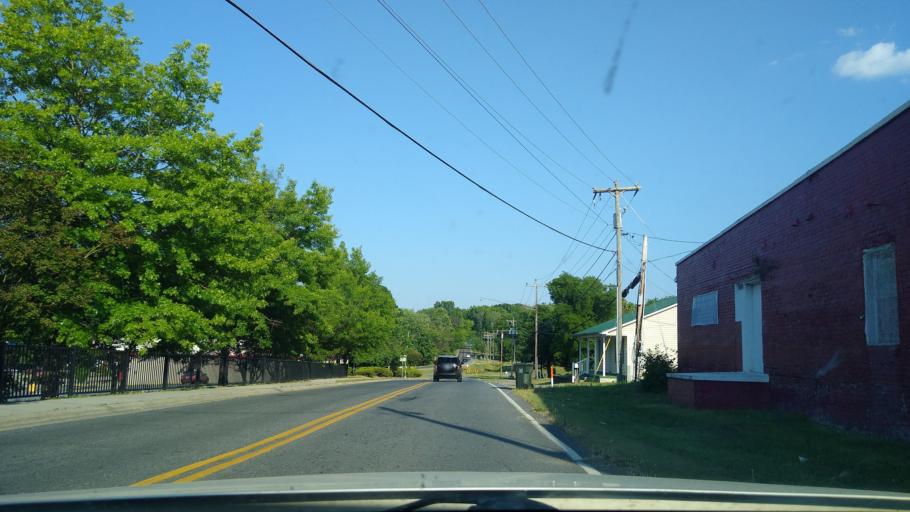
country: US
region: North Carolina
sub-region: Guilford County
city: Greensboro
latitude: 36.0398
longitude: -79.7710
